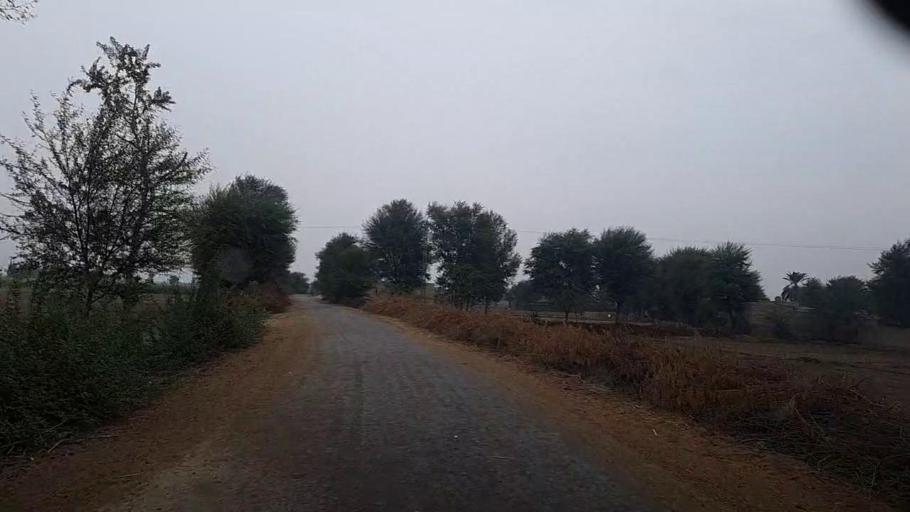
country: PK
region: Sindh
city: Ranipur
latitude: 27.2635
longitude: 68.5712
